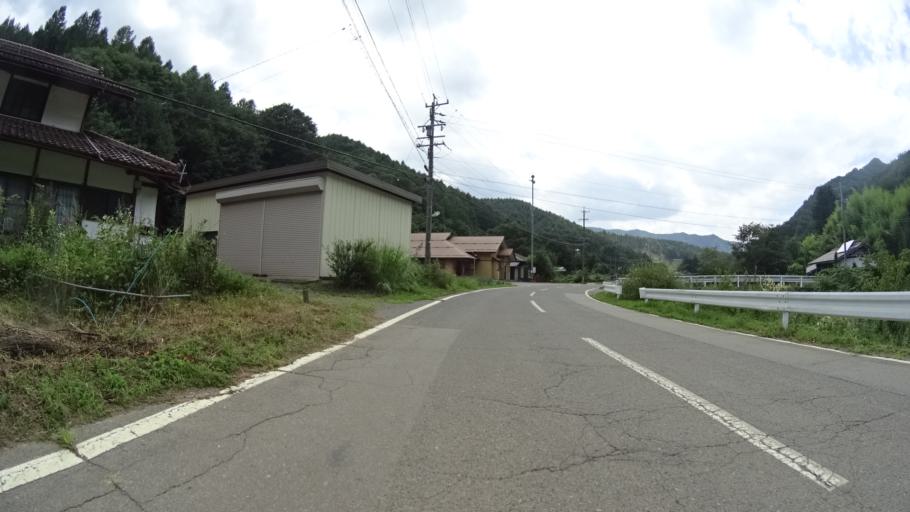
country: JP
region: Nagano
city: Saku
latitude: 36.0652
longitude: 138.5889
